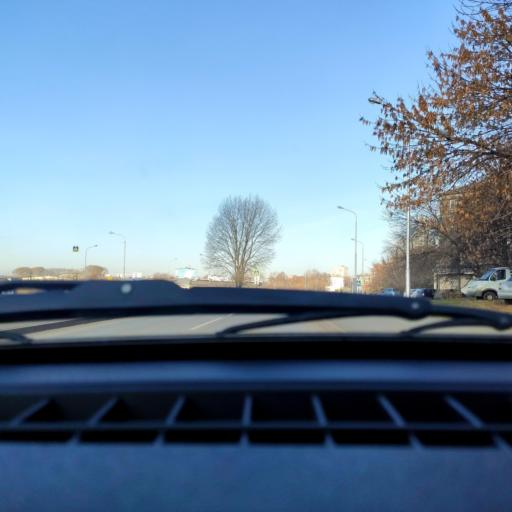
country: RU
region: Bashkortostan
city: Ufa
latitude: 54.8016
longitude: 56.1151
